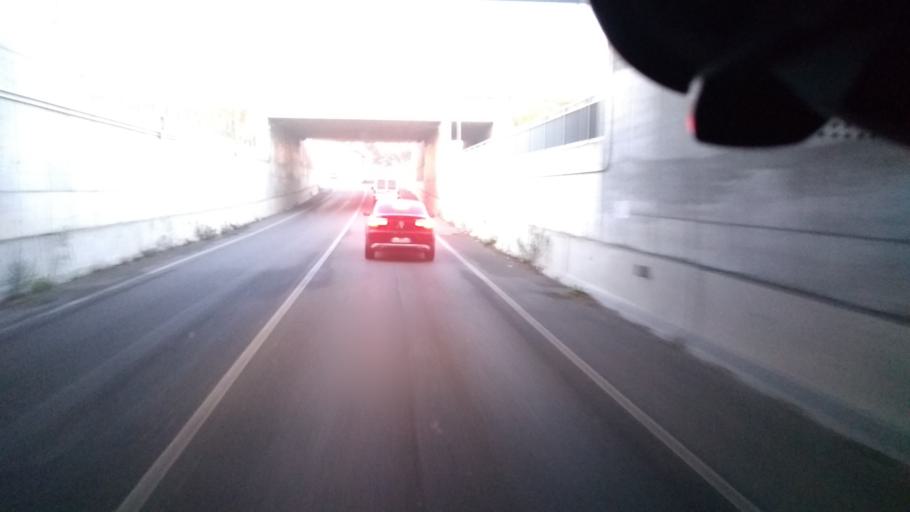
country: IT
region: Lombardy
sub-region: Provincia di Bergamo
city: Calvenzano
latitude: 45.5035
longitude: 9.5971
